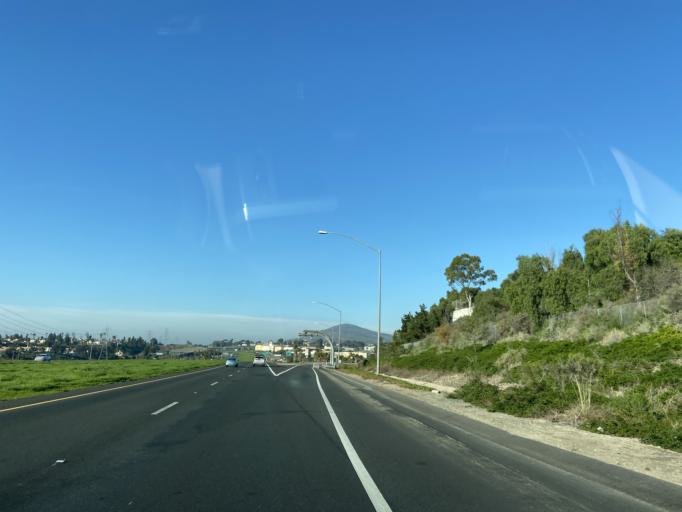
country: US
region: California
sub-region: San Diego County
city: Bonita
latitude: 32.6414
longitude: -116.9705
